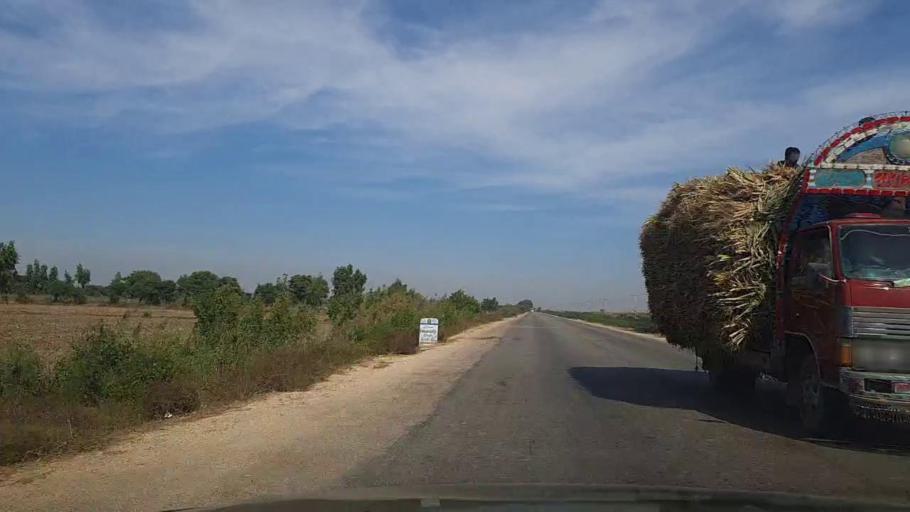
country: PK
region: Sindh
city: Daro Mehar
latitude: 24.9495
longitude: 68.1127
